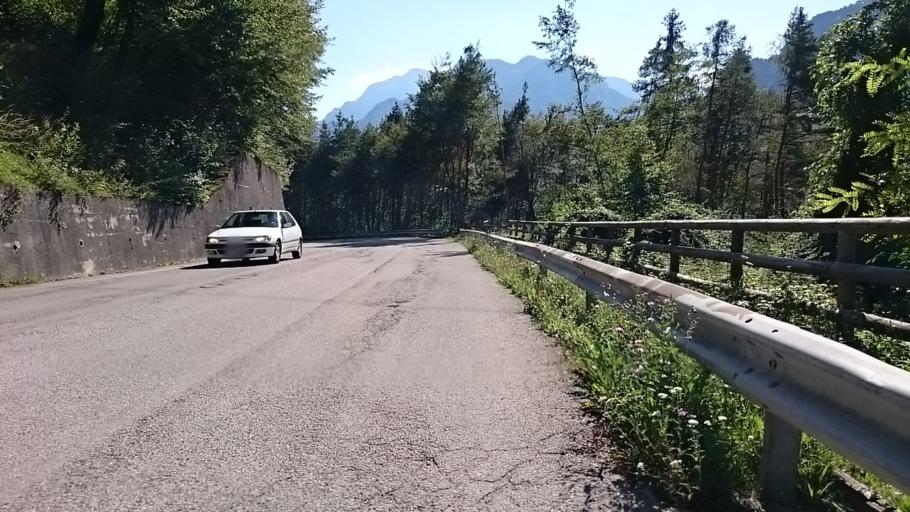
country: IT
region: Veneto
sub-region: Provincia di Belluno
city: Longarone
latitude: 46.2503
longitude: 12.3138
